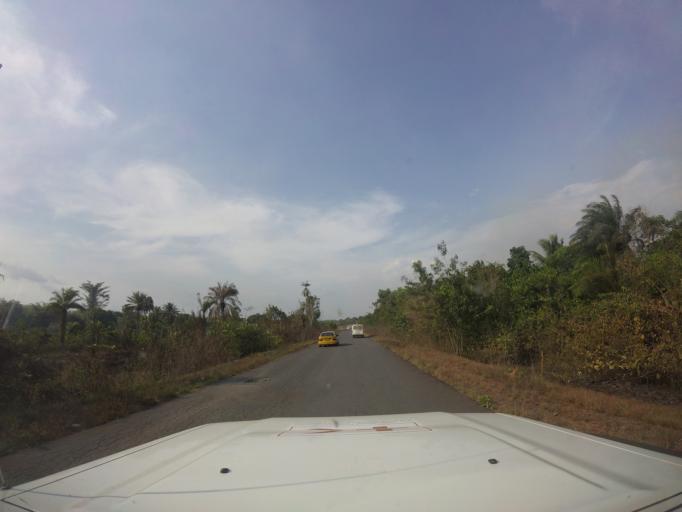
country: LR
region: Bomi
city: Tubmanburg
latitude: 6.7543
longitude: -10.8522
